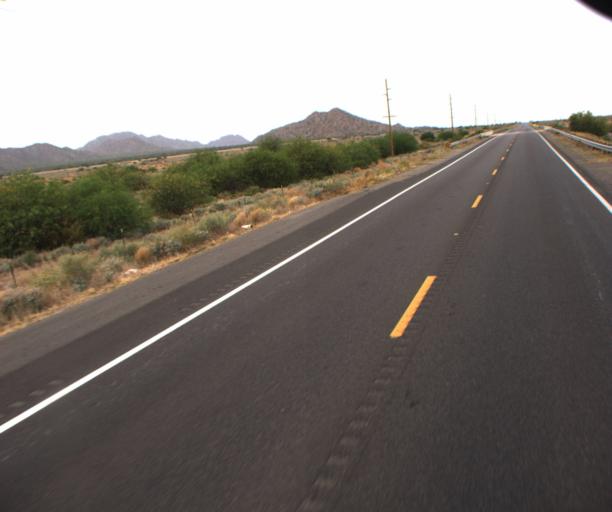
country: US
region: Arizona
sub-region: Pinal County
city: Blackwater
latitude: 33.0121
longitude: -111.6236
